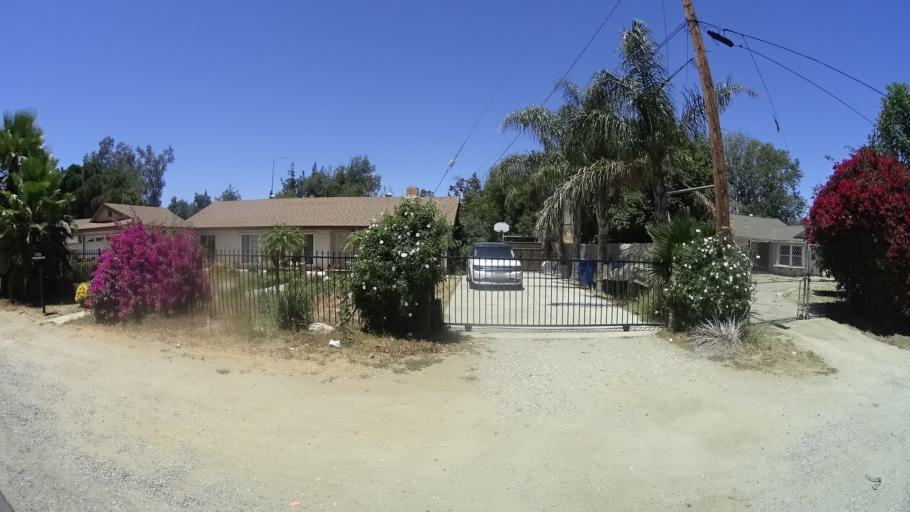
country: US
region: California
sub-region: Los Angeles County
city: San Fernando
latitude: 34.2401
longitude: -118.4719
